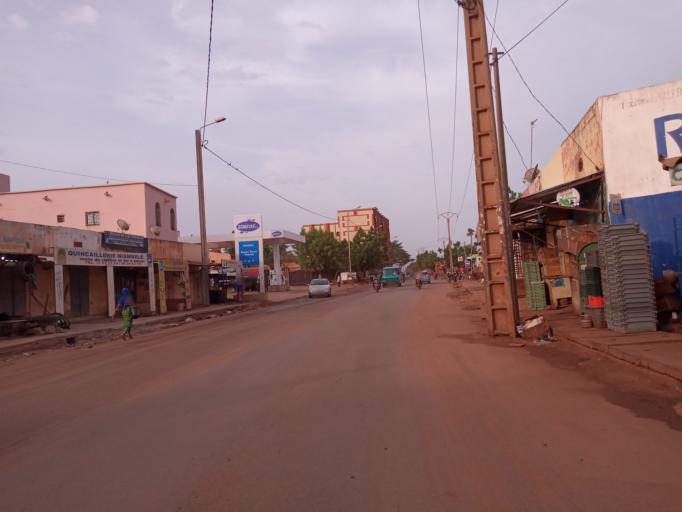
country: ML
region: Bamako
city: Bamako
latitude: 12.5818
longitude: -8.0238
